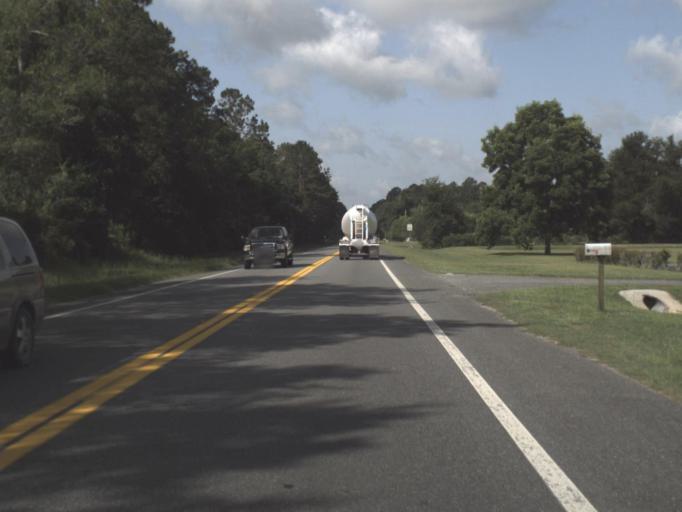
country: US
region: Florida
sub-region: Columbia County
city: Lake City
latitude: 30.1541
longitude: -82.6920
